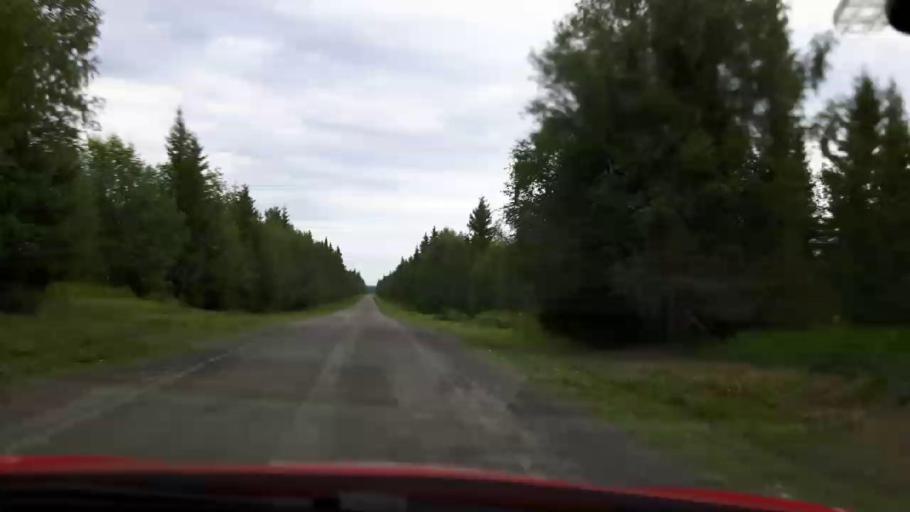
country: SE
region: Jaemtland
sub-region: Stroemsunds Kommun
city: Stroemsund
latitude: 63.7231
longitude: 15.5392
